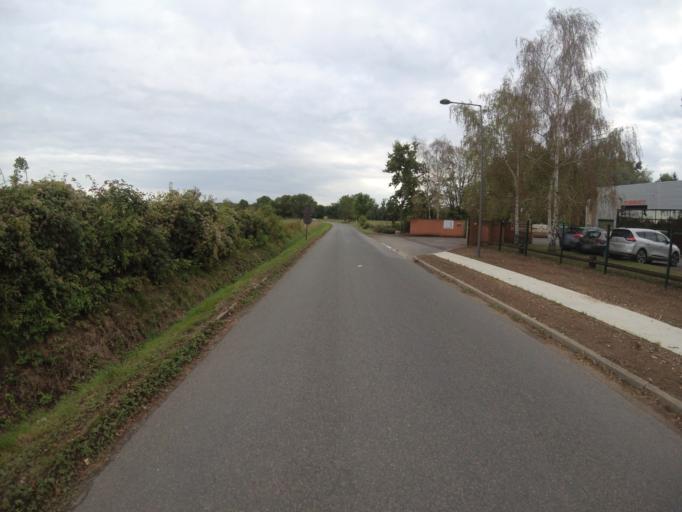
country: FR
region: Ile-de-France
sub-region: Departement de Seine-et-Marne
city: Saint-Thibault-des-Vignes
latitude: 48.8617
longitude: 2.6768
